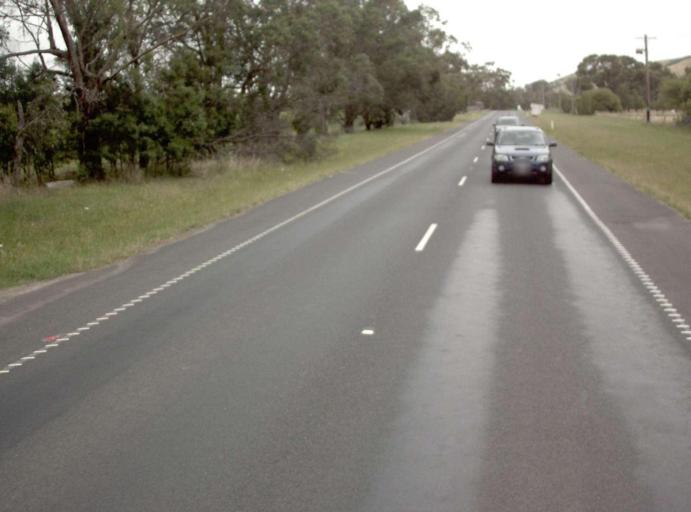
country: AU
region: Victoria
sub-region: Yarra Ranges
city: Yarra Glen
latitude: -37.6089
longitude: 145.4152
